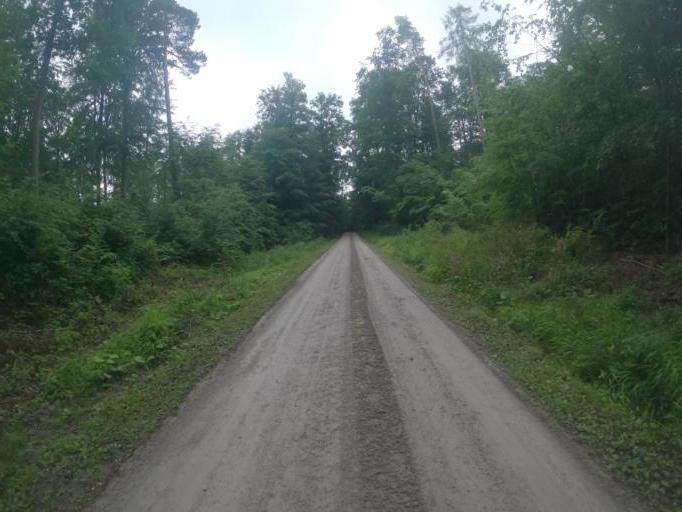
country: DE
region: Baden-Wuerttemberg
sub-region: Regierungsbezirk Stuttgart
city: Schorndorf
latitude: 48.7645
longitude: 9.5389
